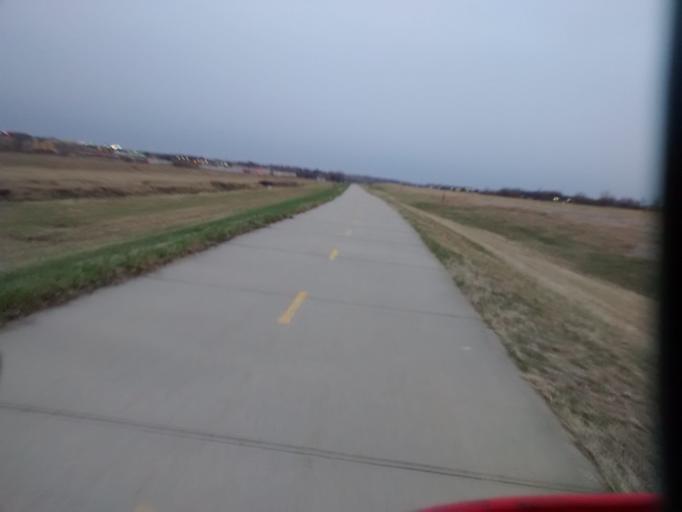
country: US
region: Nebraska
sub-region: Sarpy County
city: Offutt Air Force Base
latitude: 41.1442
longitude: -95.9533
